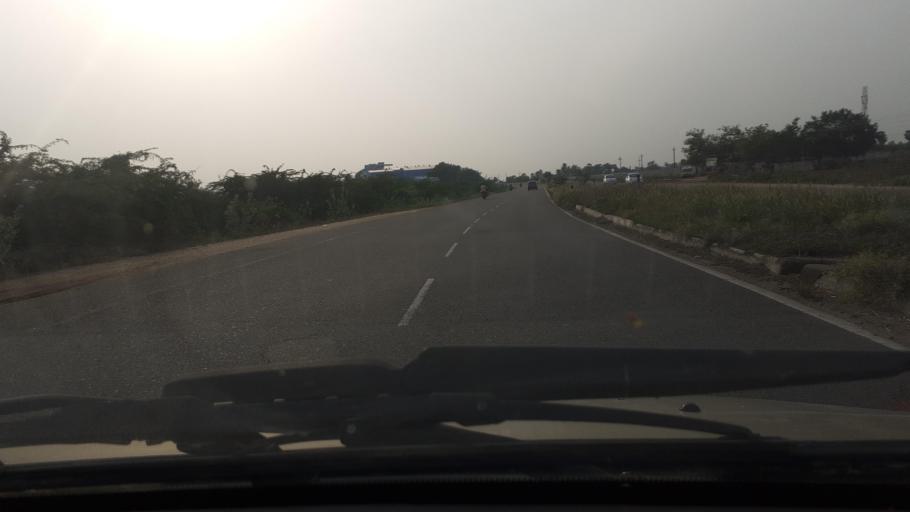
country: IN
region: Tamil Nadu
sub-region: Tirunelveli Kattabo
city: Tirunelveli
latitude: 8.7082
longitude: 77.8107
